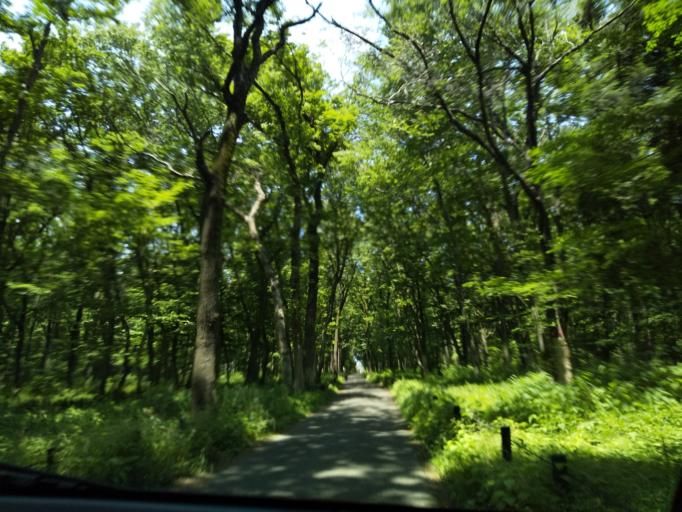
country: JP
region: Tokyo
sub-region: Machida-shi
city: Machida
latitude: 35.5409
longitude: 139.4080
